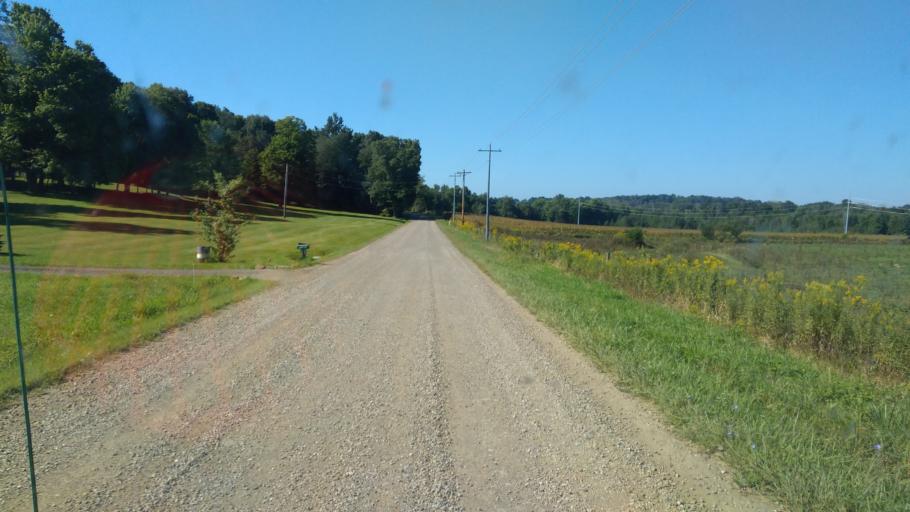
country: US
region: Ohio
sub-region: Knox County
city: Fredericktown
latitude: 40.4872
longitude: -82.4562
